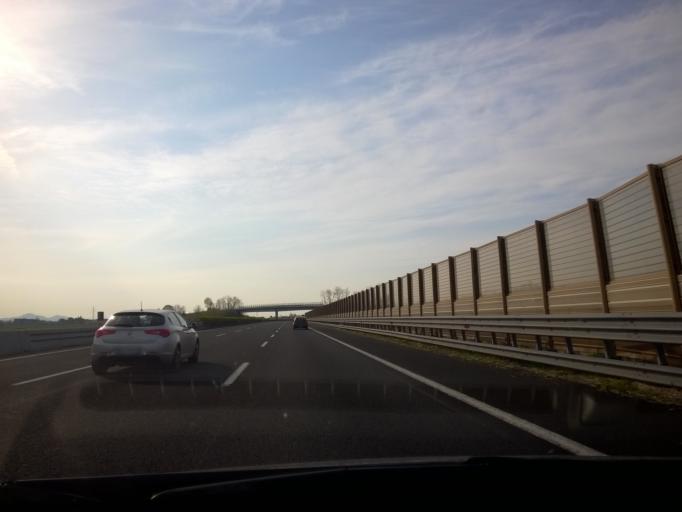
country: IT
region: Emilia-Romagna
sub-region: Forli-Cesena
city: Bagnarola
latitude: 44.1450
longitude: 12.3320
